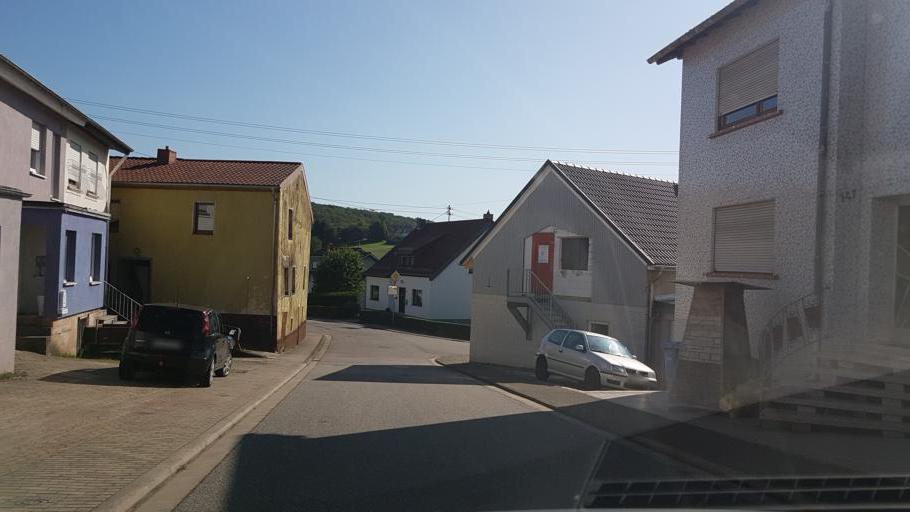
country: DE
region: Saarland
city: Lebach
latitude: 49.4766
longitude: 6.9031
